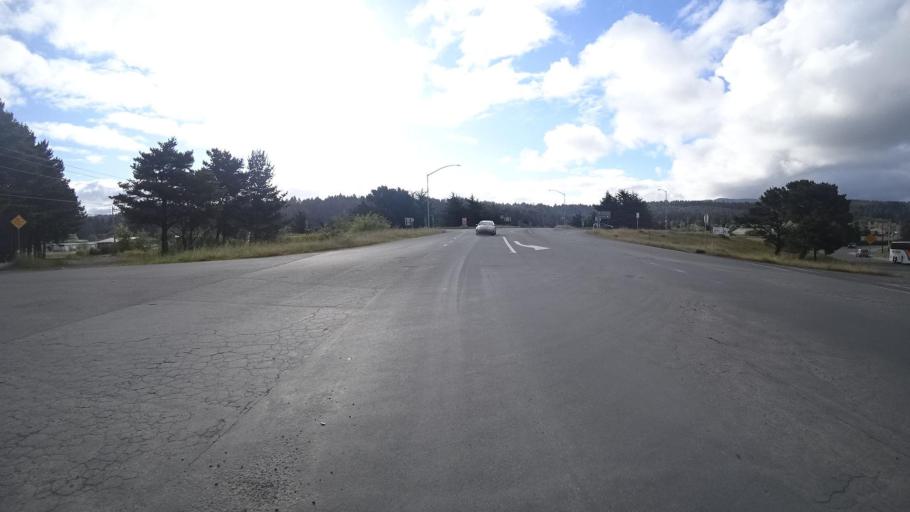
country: US
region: California
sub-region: Humboldt County
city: Arcata
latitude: 40.9049
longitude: -124.0752
